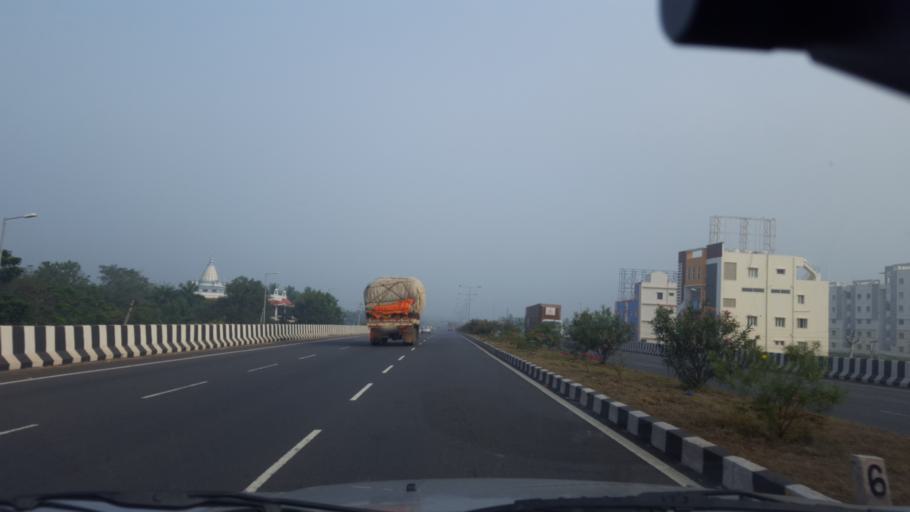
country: IN
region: Andhra Pradesh
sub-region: Prakasam
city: Ongole
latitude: 15.4577
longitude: 80.0480
